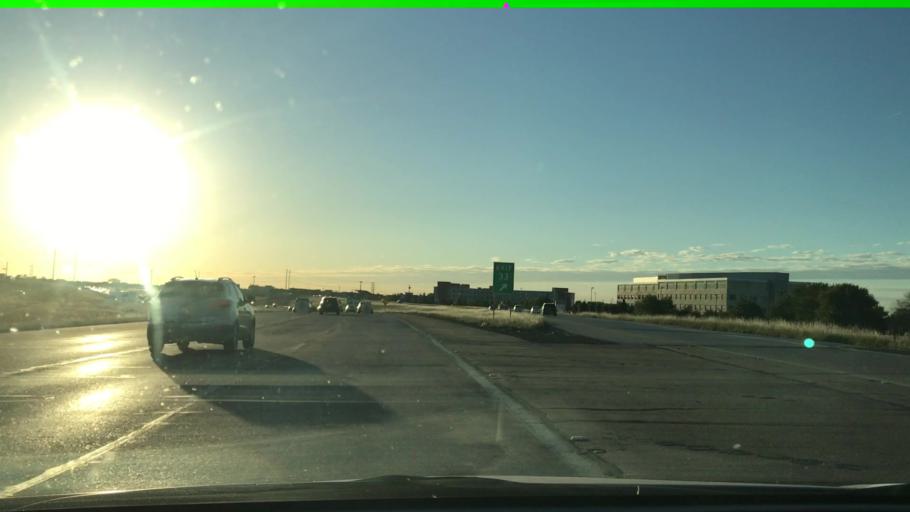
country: US
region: Texas
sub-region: Dallas County
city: Coppell
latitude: 32.9256
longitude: -96.9997
